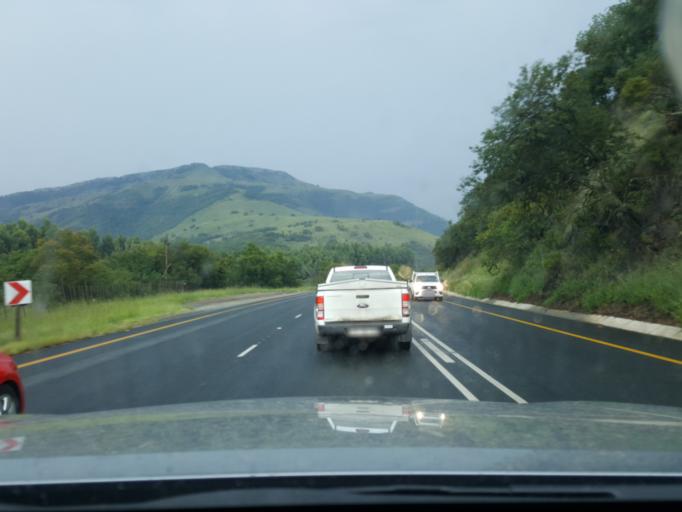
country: ZA
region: Mpumalanga
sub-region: Nkangala District Municipality
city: Belfast
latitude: -25.6220
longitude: 30.3995
